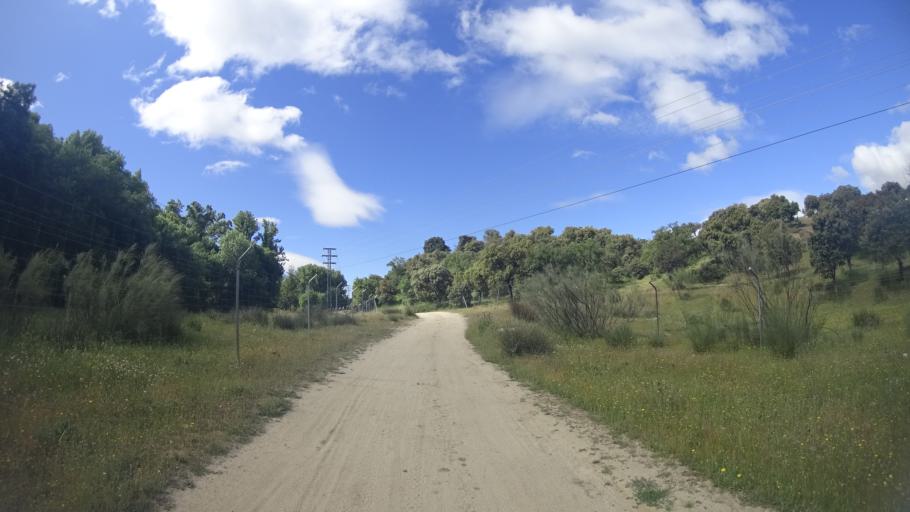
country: ES
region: Madrid
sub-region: Provincia de Madrid
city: Villanueva del Pardillo
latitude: 40.4353
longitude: -3.9524
